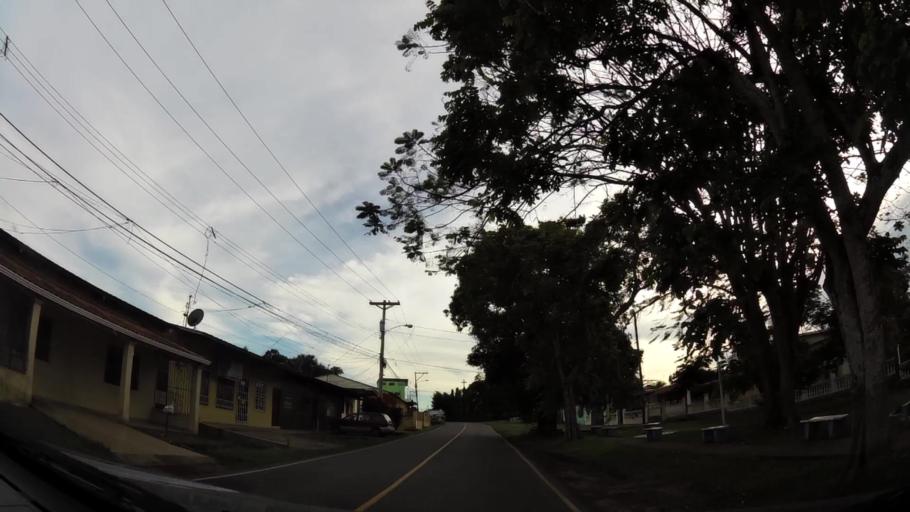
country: PA
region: Panama
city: La Chorrera
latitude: 8.8855
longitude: -79.7796
